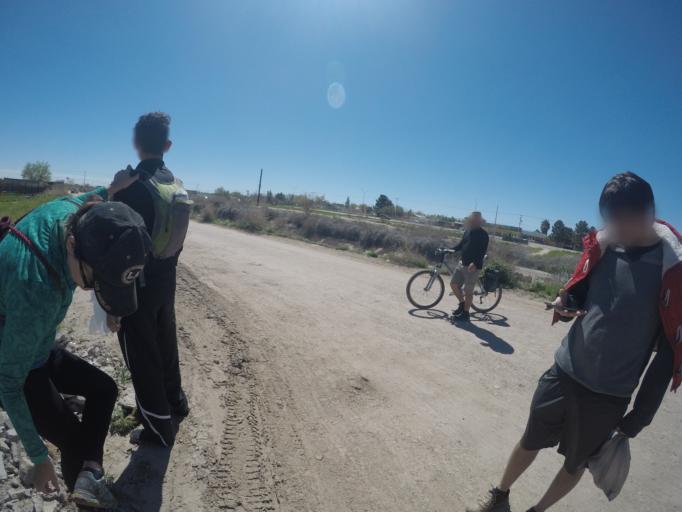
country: US
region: Texas
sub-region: El Paso County
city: Socorro Mission Number 1 Colonia
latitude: 31.6074
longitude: -106.3117
